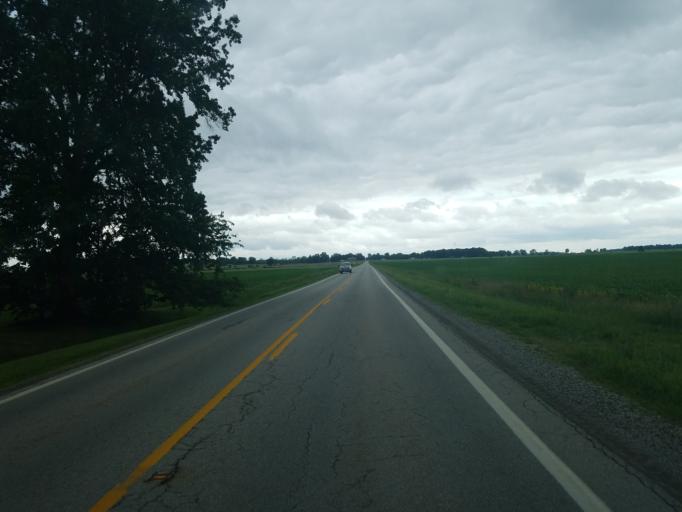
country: US
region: Ohio
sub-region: Marion County
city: Marion
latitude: 40.6744
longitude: -83.1479
